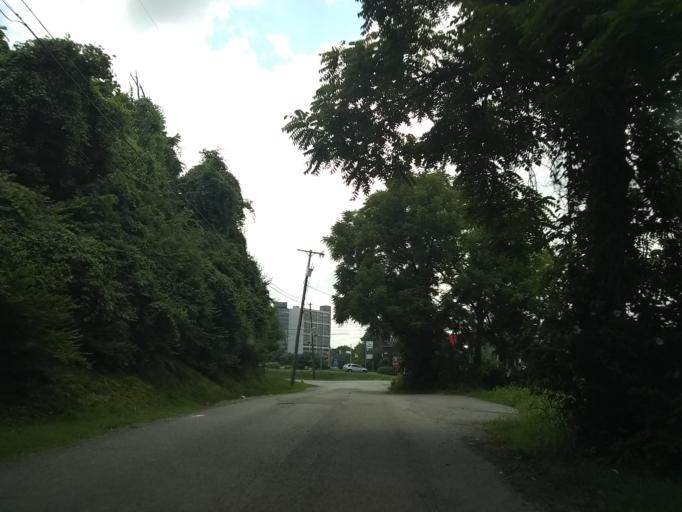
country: US
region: Tennessee
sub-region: Davidson County
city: Nashville
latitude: 36.1526
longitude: -86.6858
